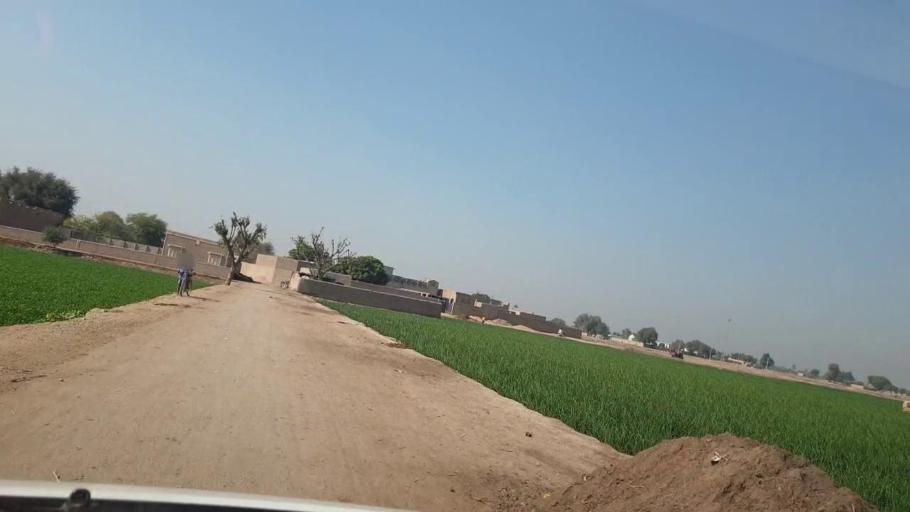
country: PK
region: Sindh
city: Bhan
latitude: 26.6457
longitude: 67.7022
